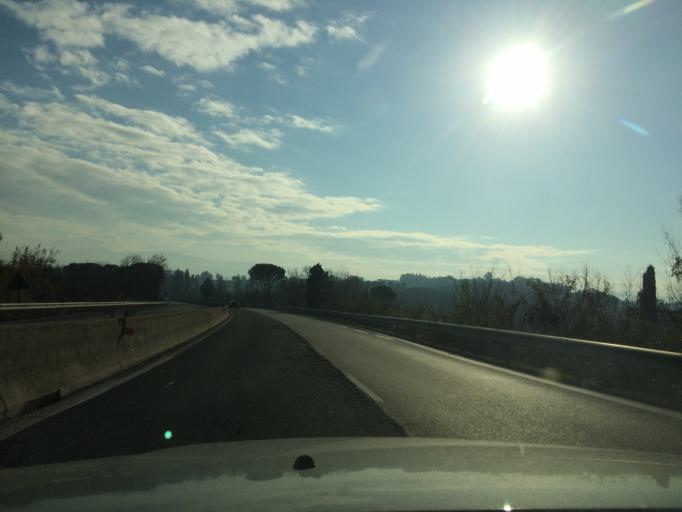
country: IT
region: Umbria
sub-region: Provincia di Terni
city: San Gemini
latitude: 42.5958
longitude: 12.5631
